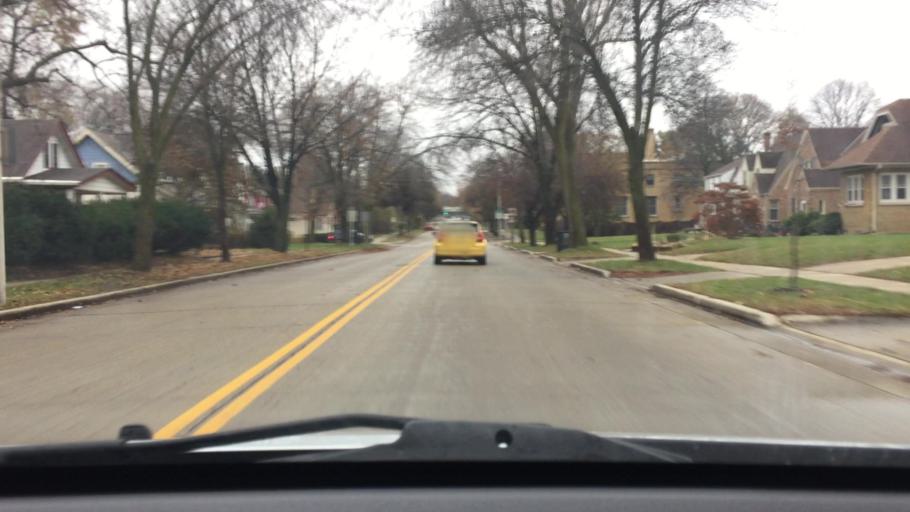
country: US
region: Wisconsin
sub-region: Milwaukee County
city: Wauwatosa
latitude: 43.0348
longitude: -87.9974
